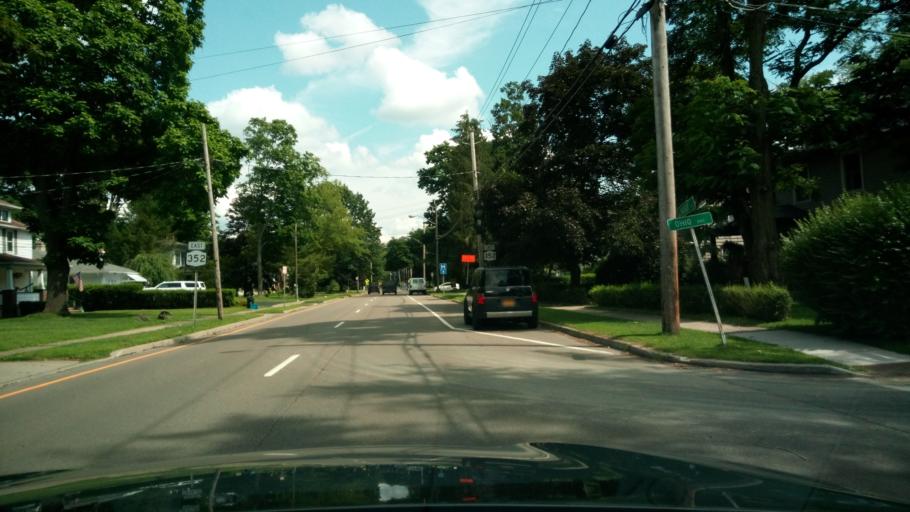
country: US
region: New York
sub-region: Chemung County
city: West Elmira
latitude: 42.0802
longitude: -76.8563
